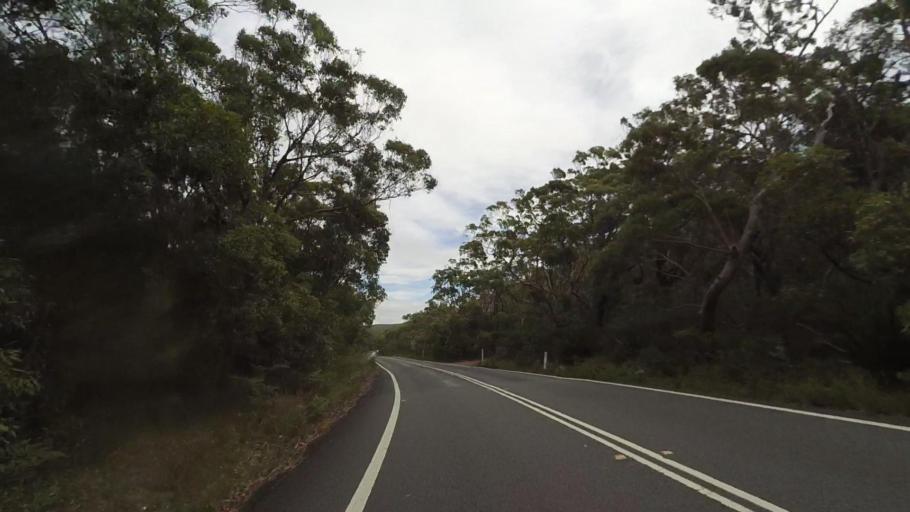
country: AU
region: New South Wales
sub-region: Sutherland Shire
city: Grays Point
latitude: -34.1192
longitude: 151.0732
